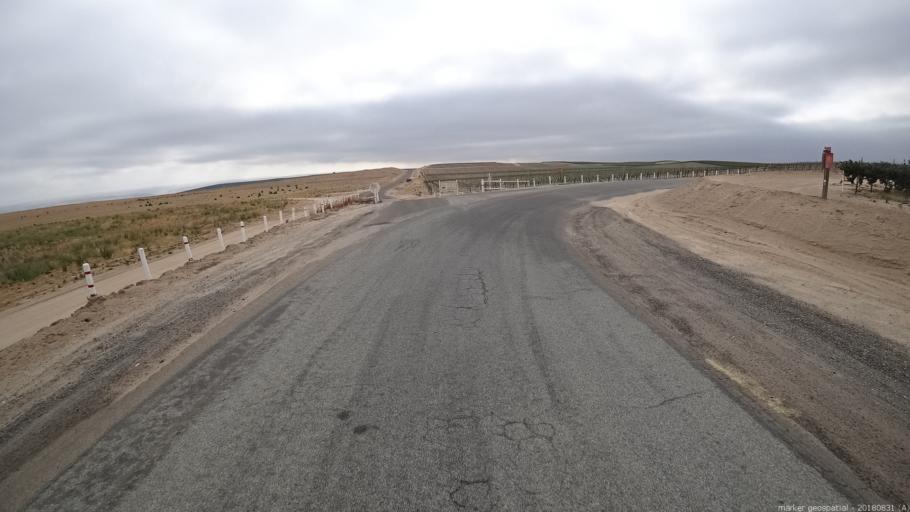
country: US
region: California
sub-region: Monterey County
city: King City
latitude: 36.1543
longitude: -121.1008
